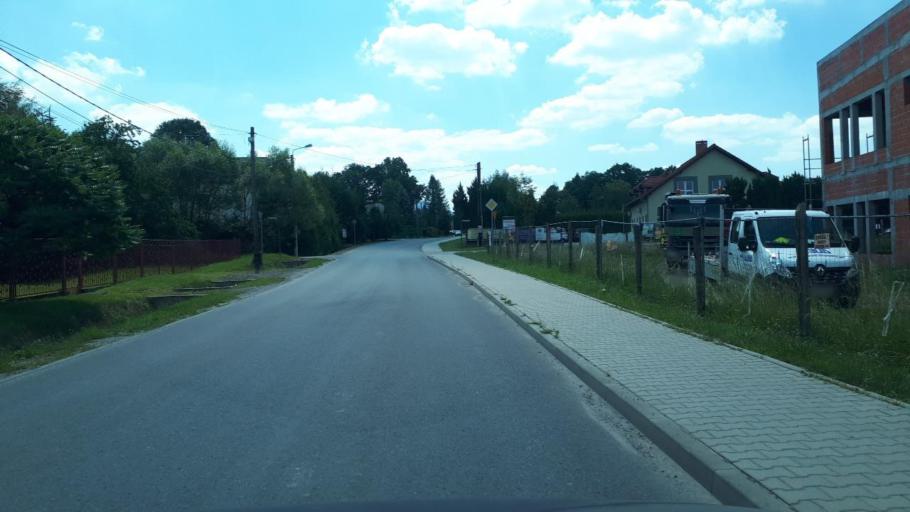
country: PL
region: Silesian Voivodeship
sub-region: Powiat bielski
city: Pisarzowice
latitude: 49.8763
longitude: 19.1414
